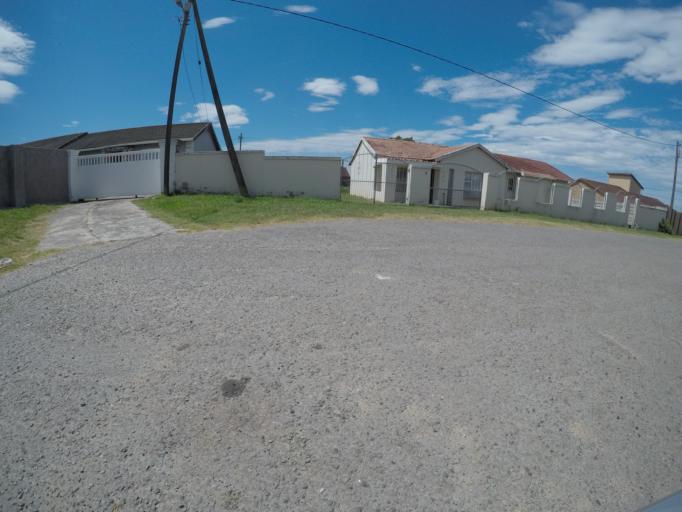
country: ZA
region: Eastern Cape
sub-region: Buffalo City Metropolitan Municipality
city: East London
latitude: -33.0432
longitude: 27.8678
